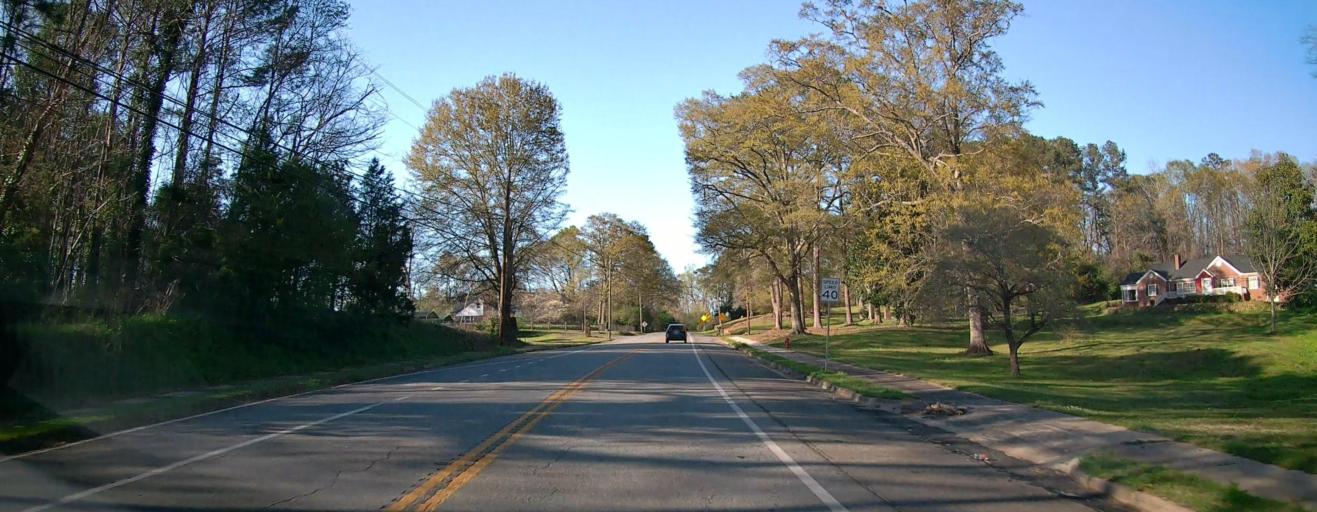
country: US
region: Georgia
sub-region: Butts County
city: Indian Springs
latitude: 33.2478
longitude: -83.9203
